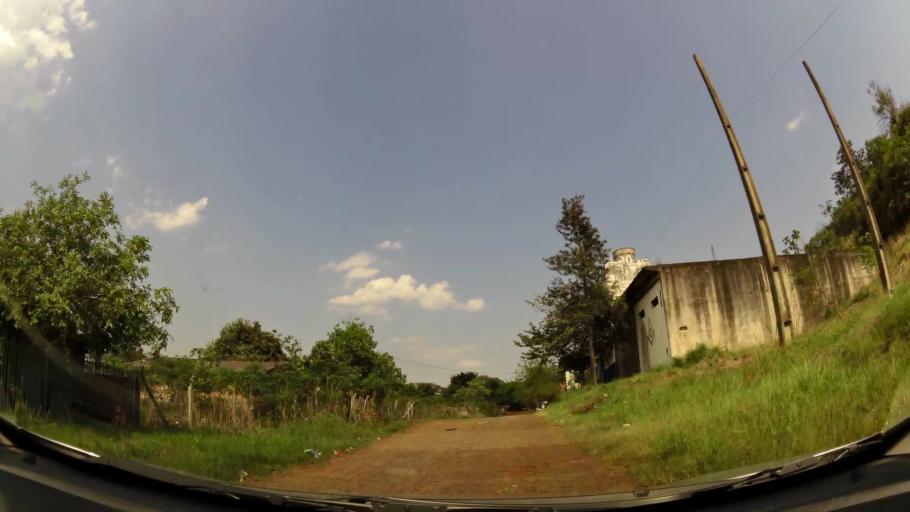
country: PY
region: Alto Parana
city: Ciudad del Este
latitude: -25.5070
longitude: -54.6269
